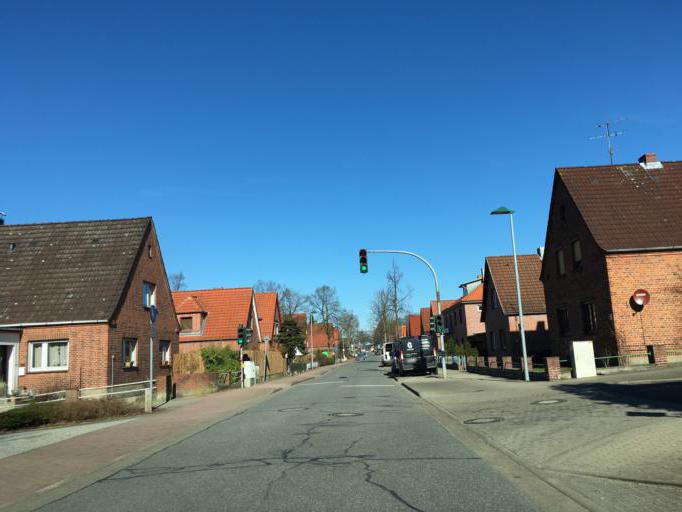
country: DE
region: Schleswig-Holstein
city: Molln
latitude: 53.6205
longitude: 10.6927
